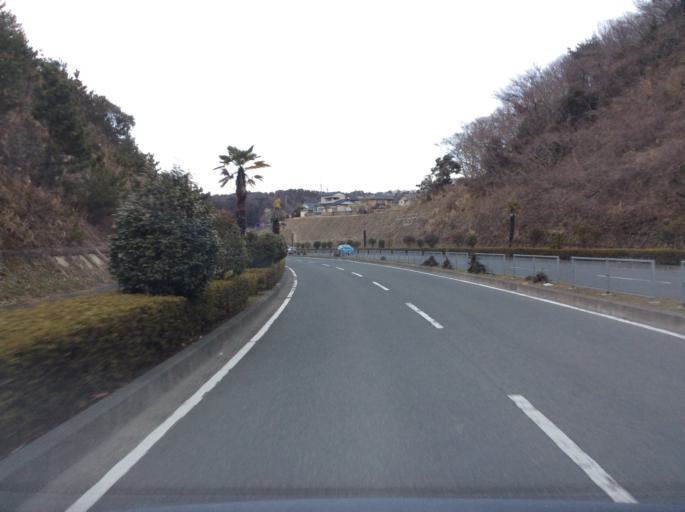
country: JP
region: Fukushima
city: Iwaki
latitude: 36.9465
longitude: 140.9201
